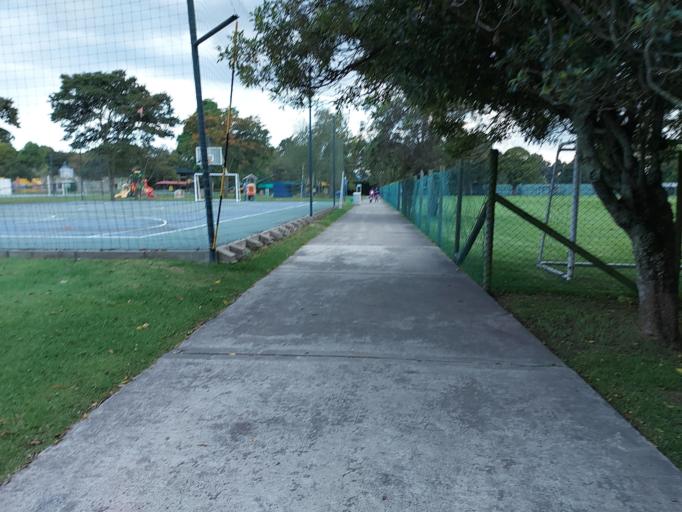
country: CO
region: Cundinamarca
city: Cota
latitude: 4.7925
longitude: -74.0450
